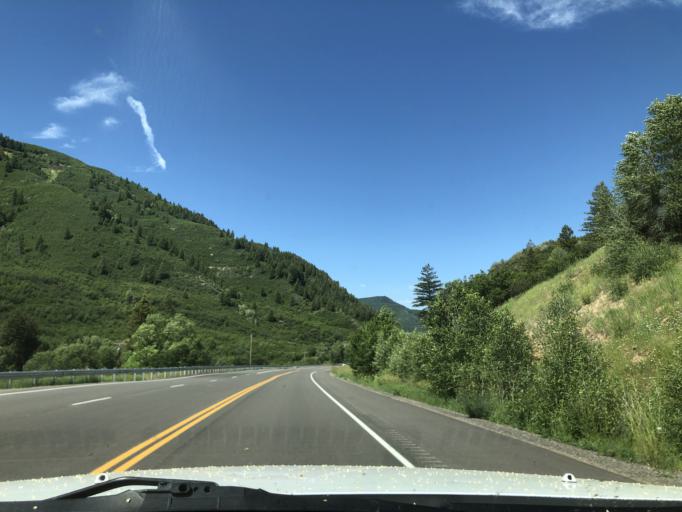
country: US
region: Colorado
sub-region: Delta County
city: Paonia
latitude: 38.9319
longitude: -107.4058
